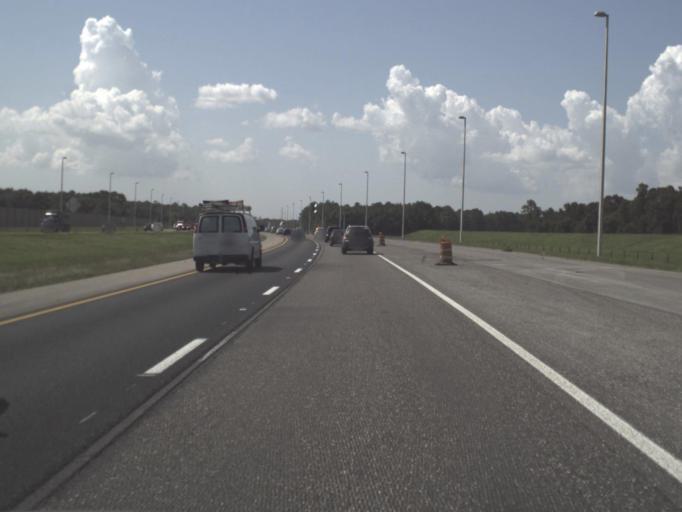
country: US
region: Florida
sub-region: Hillsborough County
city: Pebble Creek
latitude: 28.0945
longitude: -82.3579
